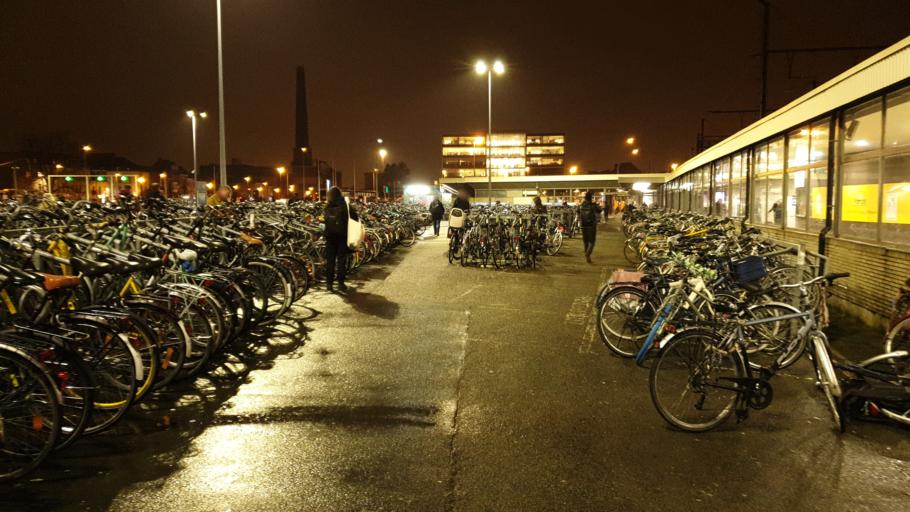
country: BE
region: Flanders
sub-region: Provincie Oost-Vlaanderen
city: Ledeberg
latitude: 51.0554
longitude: 3.7405
